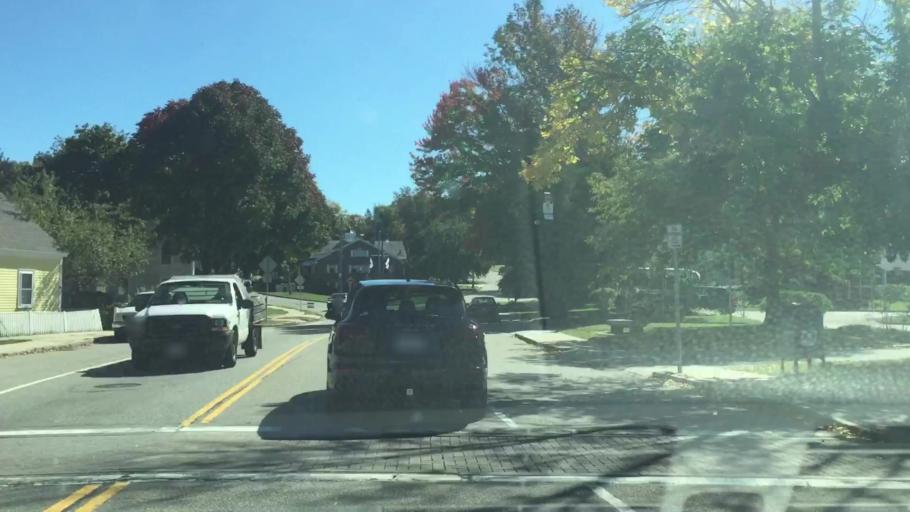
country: US
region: Massachusetts
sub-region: Essex County
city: North Andover
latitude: 42.6834
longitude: -71.1123
